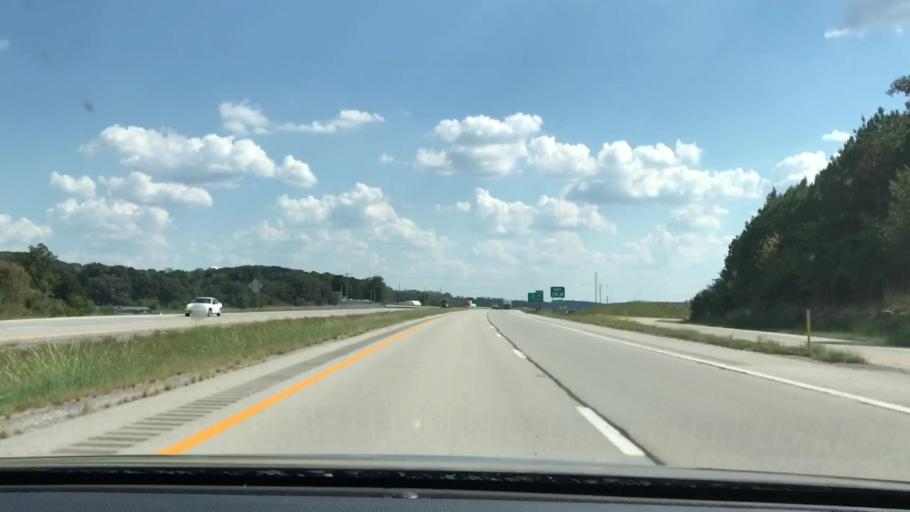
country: US
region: Kentucky
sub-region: Butler County
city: Morgantown
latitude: 37.2178
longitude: -86.7132
